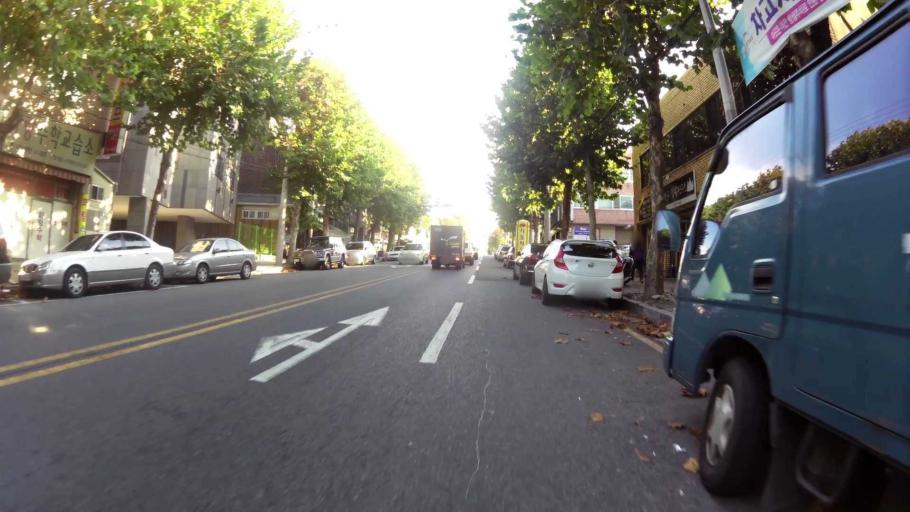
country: KR
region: Daegu
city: Daegu
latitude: 35.8633
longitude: 128.6395
